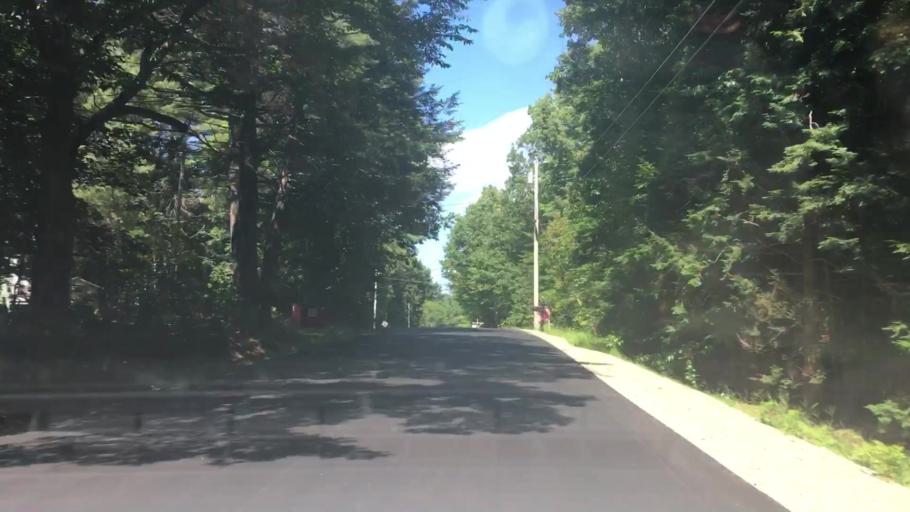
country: US
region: Maine
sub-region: Androscoggin County
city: Sabattus
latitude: 44.1303
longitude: -70.0189
